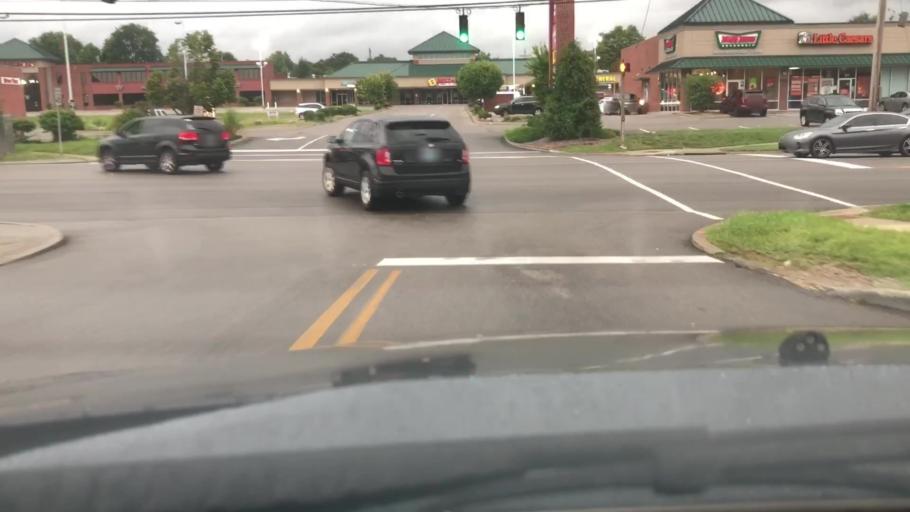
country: US
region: Kentucky
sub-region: Jefferson County
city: Hurstbourne Acres
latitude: 38.2051
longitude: -85.5800
